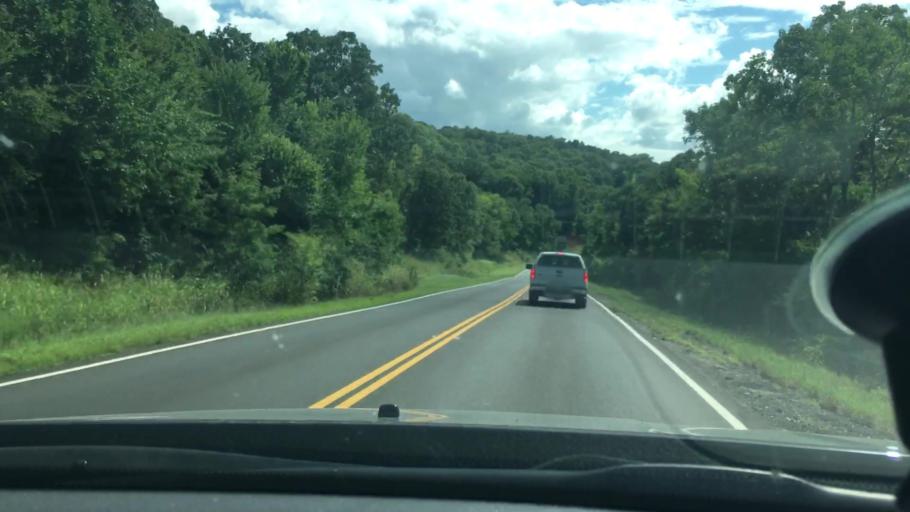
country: US
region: Oklahoma
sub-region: Sequoyah County
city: Vian
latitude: 35.6517
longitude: -94.9536
